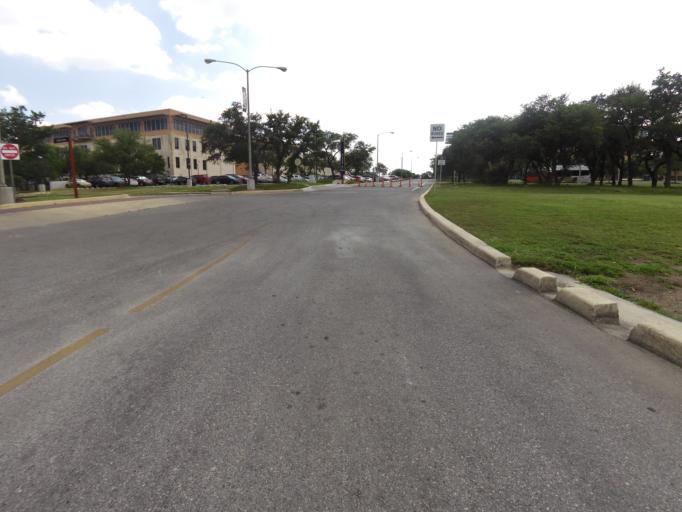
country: US
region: Texas
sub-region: Bexar County
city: Shavano Park
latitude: 29.5864
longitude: -98.6176
